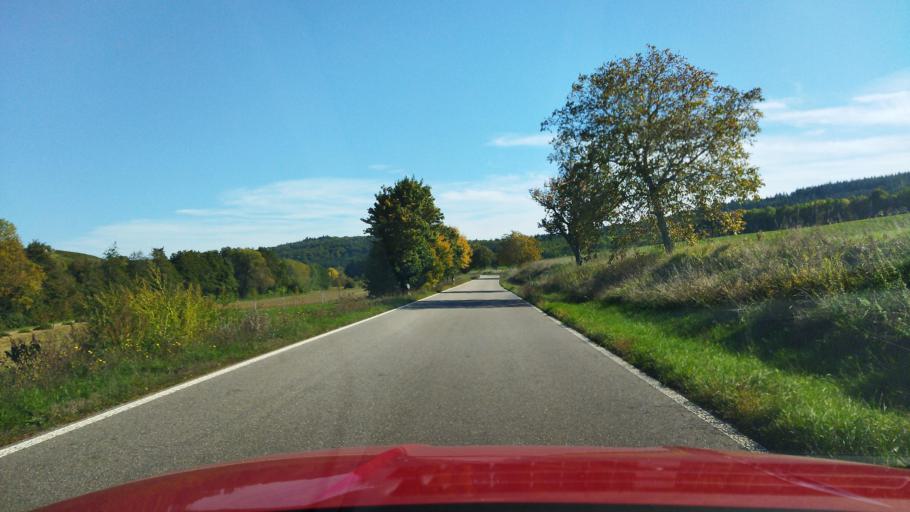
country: DE
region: Baden-Wuerttemberg
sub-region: Karlsruhe Region
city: Sulzfeld
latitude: 49.0952
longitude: 8.8671
